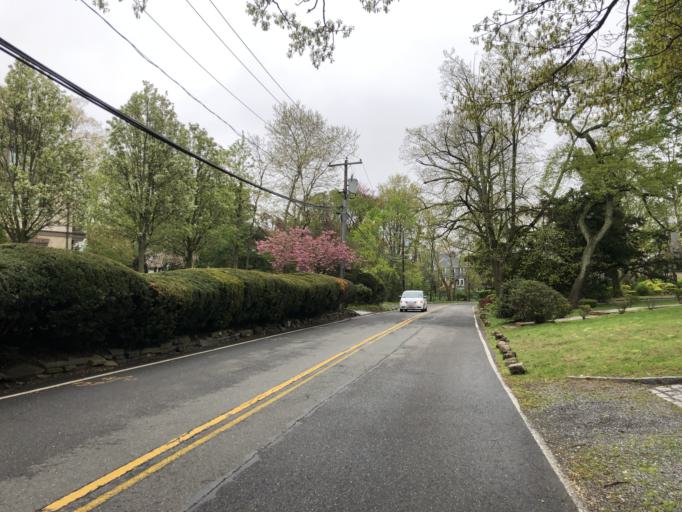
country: US
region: New York
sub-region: Nassau County
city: Woodmere
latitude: 40.6246
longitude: -73.7024
